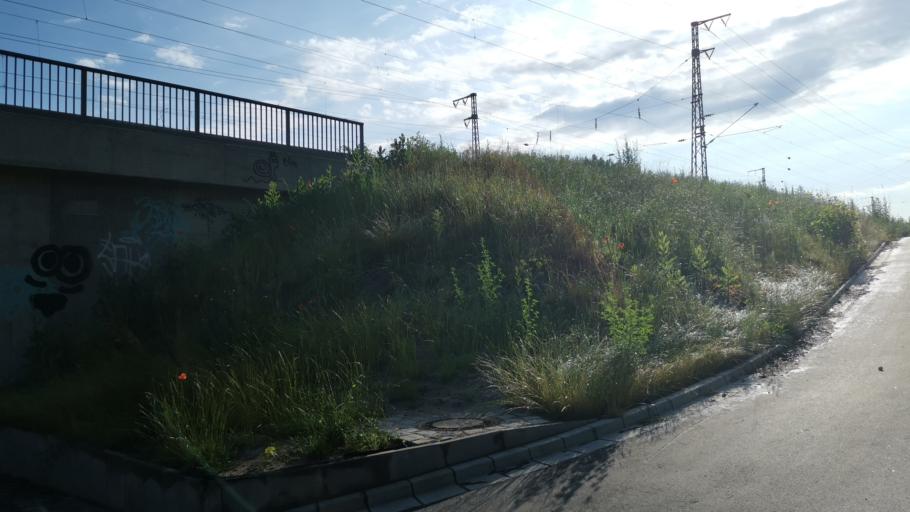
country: DE
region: Bavaria
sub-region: Regierungsbezirk Mittelfranken
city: Grossreuth bei Schweinau
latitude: 49.4229
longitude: 11.0472
